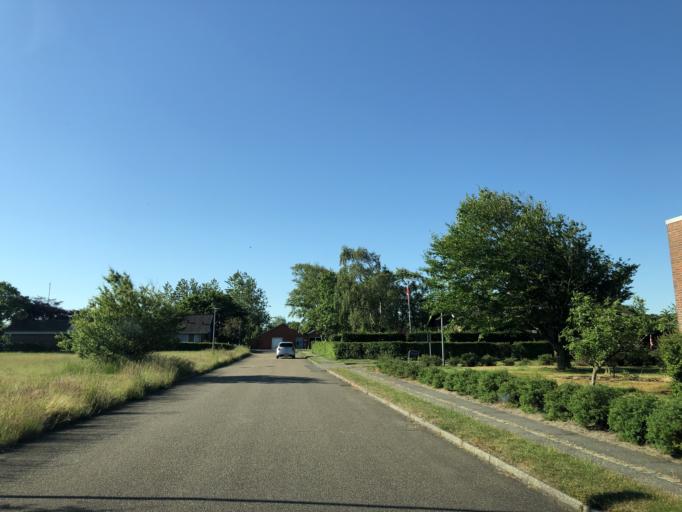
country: DK
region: Central Jutland
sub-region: Holstebro Kommune
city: Ulfborg
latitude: 56.3479
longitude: 8.3403
